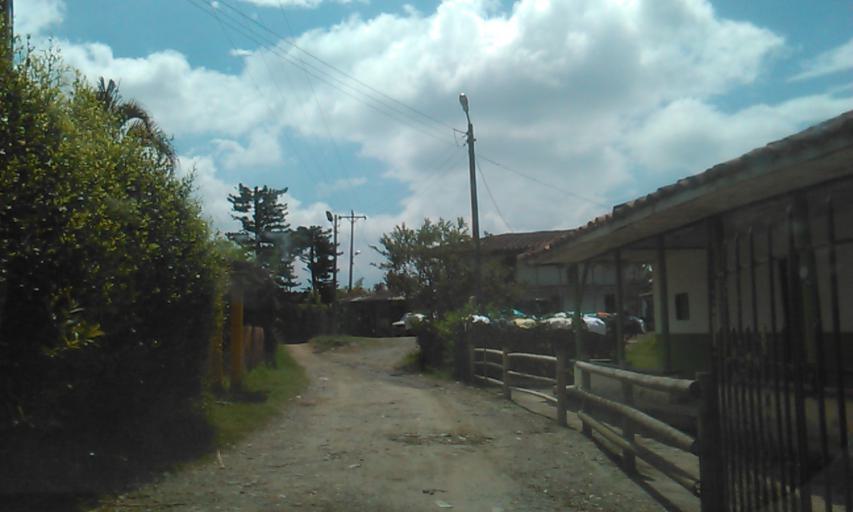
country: CO
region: Quindio
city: Circasia
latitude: 4.5916
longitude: -75.6508
